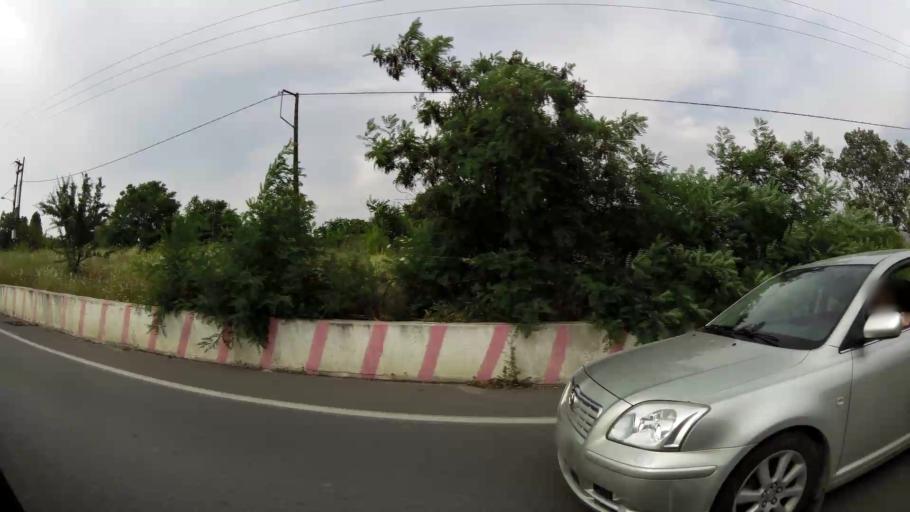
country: GR
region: Central Macedonia
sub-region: Nomos Thessalonikis
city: Oraiokastro
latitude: 40.7188
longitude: 22.9268
